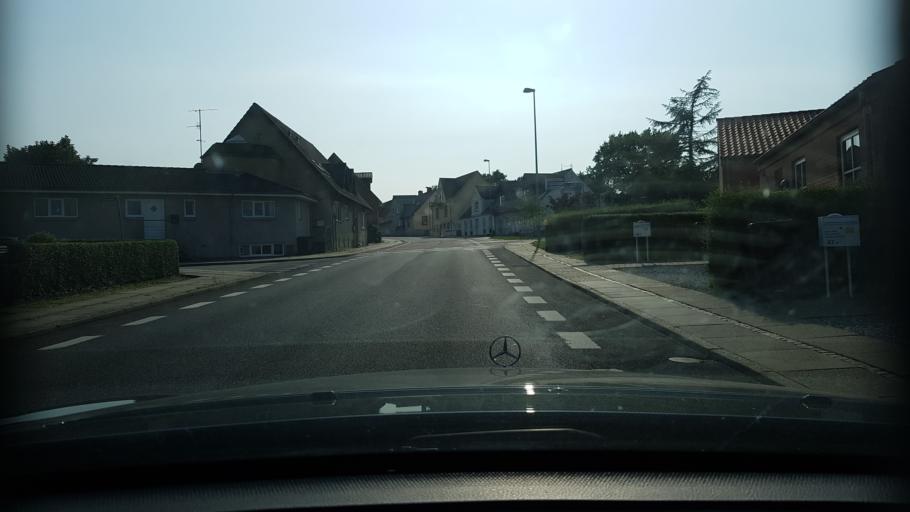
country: DK
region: North Denmark
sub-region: Mariagerfjord Kommune
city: Hadsund
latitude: 56.7217
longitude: 10.1200
